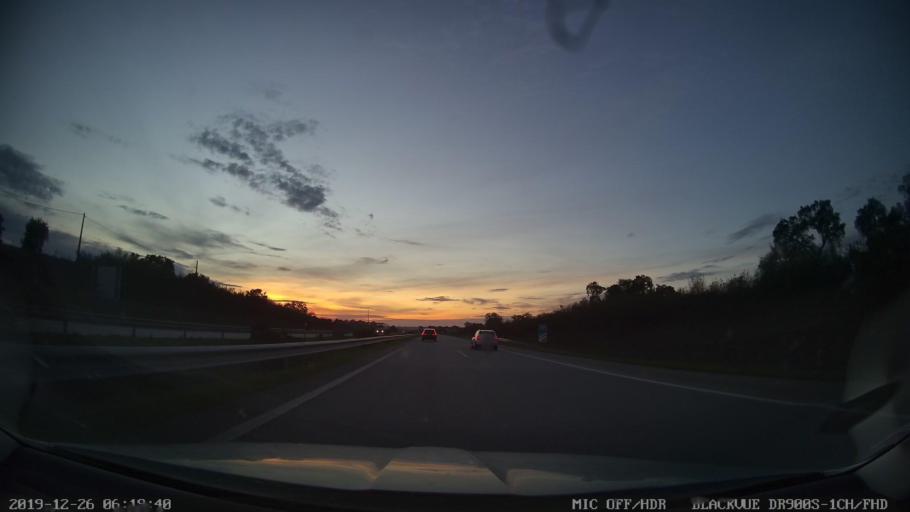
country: PT
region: Evora
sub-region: Vendas Novas
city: Vendas Novas
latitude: 38.6480
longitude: -8.4212
